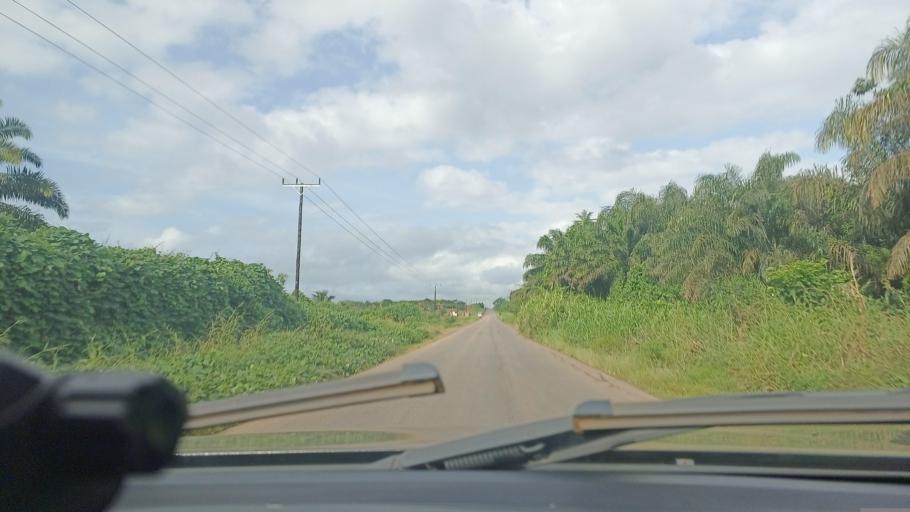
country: LR
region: Bomi
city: Tubmanburg
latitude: 6.7305
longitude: -11.0101
